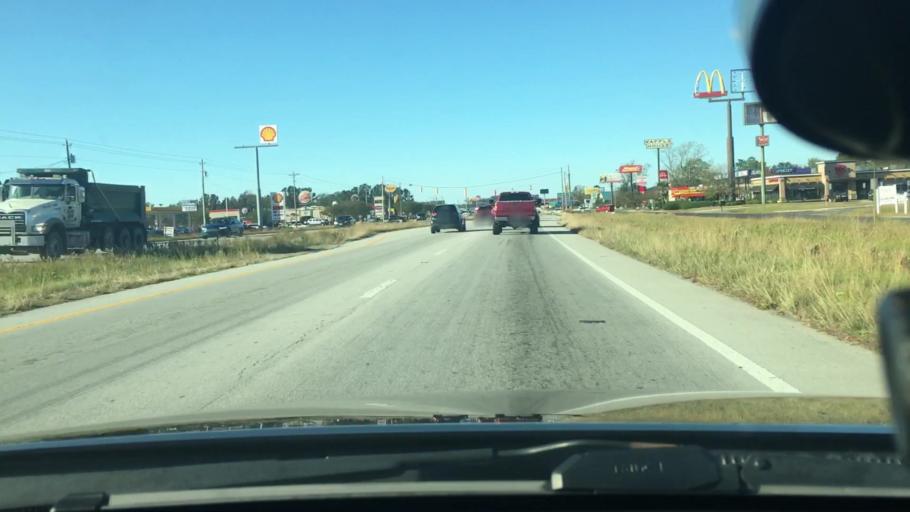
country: US
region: North Carolina
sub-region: Craven County
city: James City
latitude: 35.0800
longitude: -77.0305
